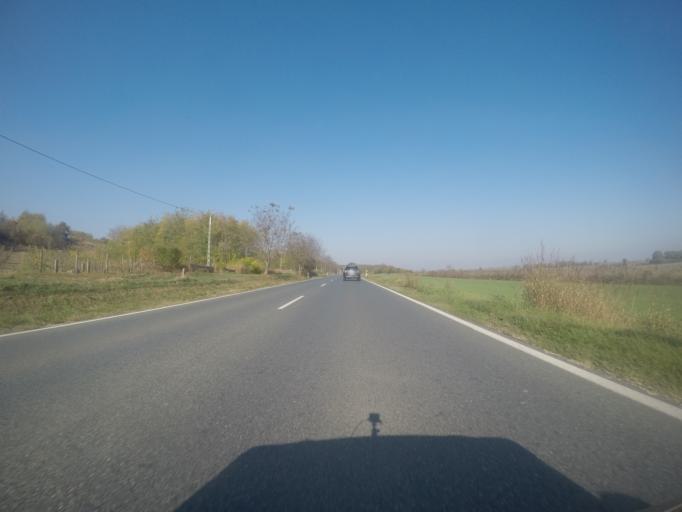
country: HU
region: Tolna
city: Paks
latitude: 46.6778
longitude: 18.8832
